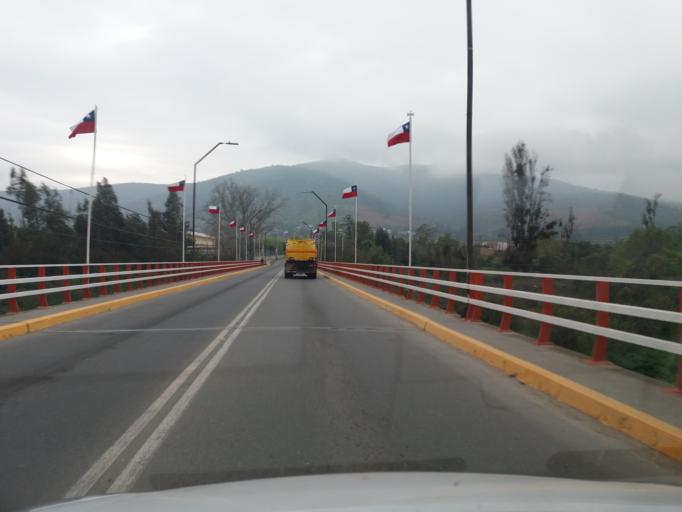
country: CL
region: Valparaiso
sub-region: Provincia de Marga Marga
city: Limache
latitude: -32.9957
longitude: -71.2667
